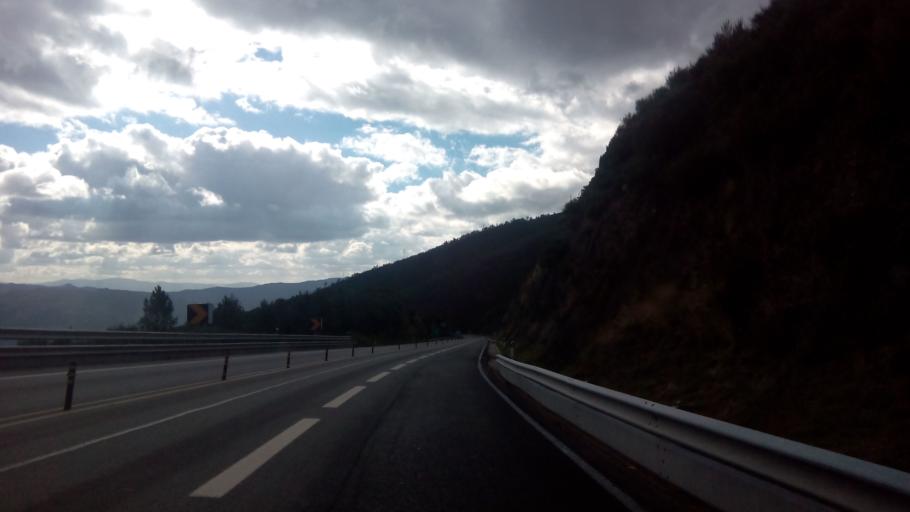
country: PT
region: Vila Real
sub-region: Mesao Frio
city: Mesao Frio
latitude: 41.2734
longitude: -7.9380
